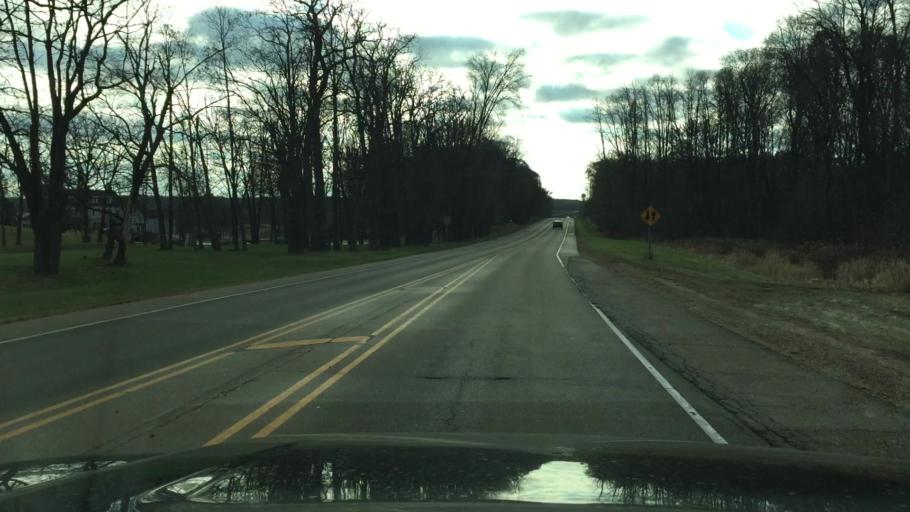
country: US
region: Wisconsin
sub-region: Walworth County
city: Williams Bay
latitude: 42.5919
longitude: -88.5338
